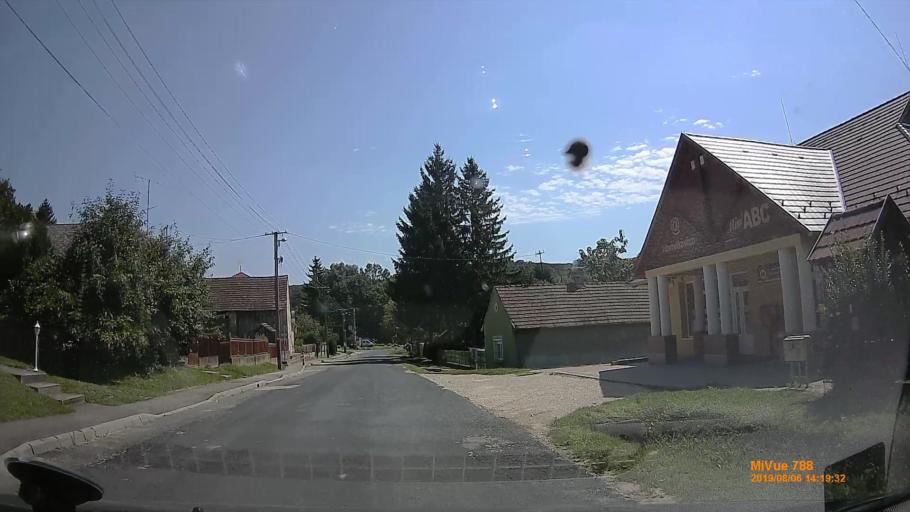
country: HU
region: Zala
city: Zalakomar
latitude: 46.5295
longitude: 17.0891
